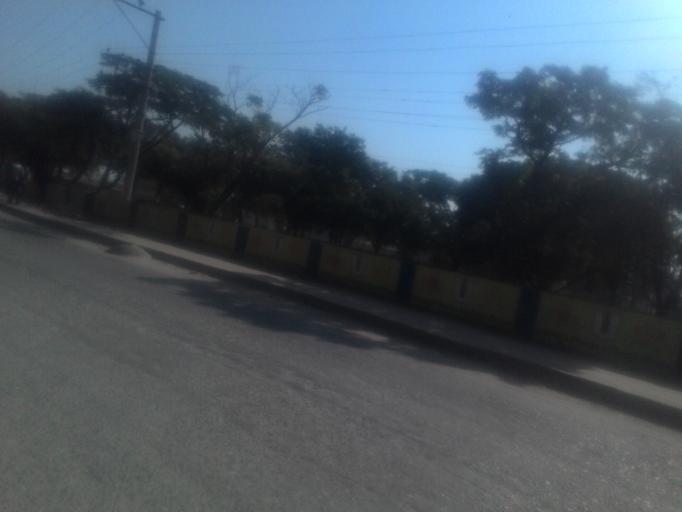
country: IN
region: Andhra Pradesh
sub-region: Chittoor
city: Madanapalle
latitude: 13.5566
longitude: 78.5030
